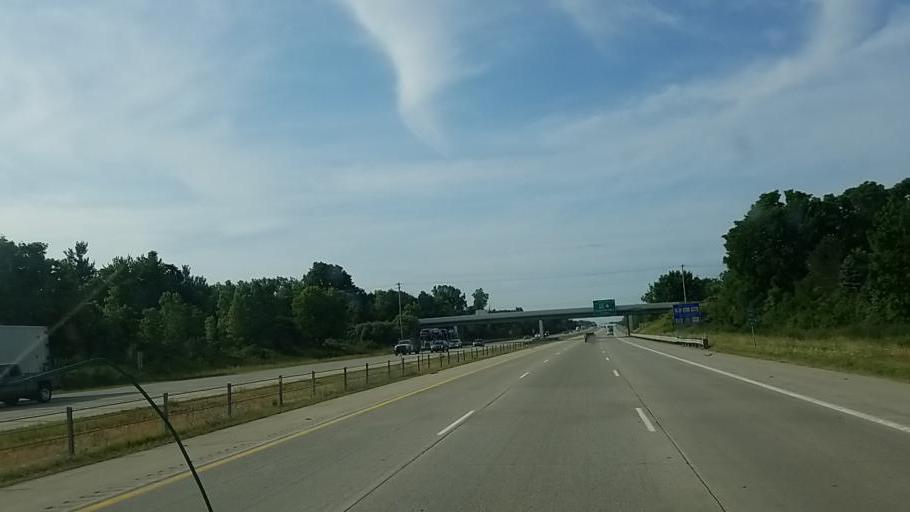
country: US
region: Michigan
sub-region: Eaton County
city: Waverly
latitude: 42.7572
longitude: -84.6677
